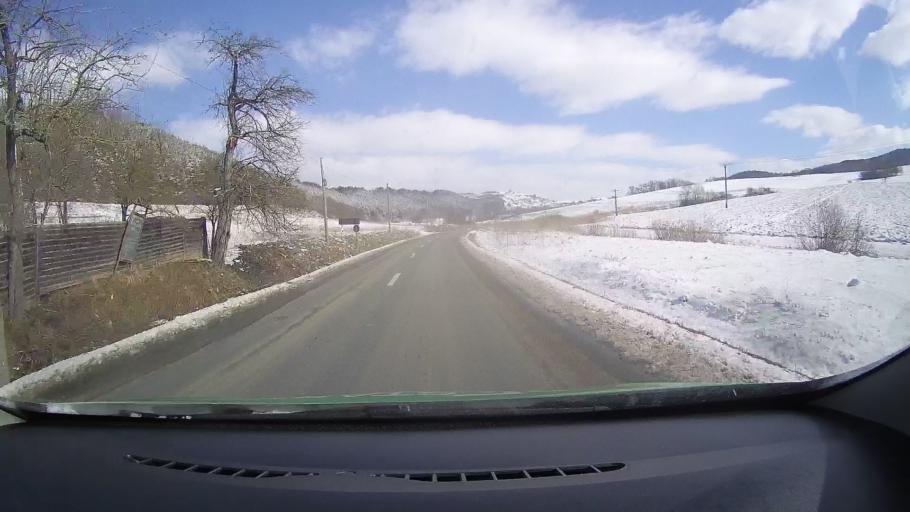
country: RO
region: Sibiu
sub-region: Comuna Barghis
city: Barghis
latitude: 45.9848
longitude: 24.4911
